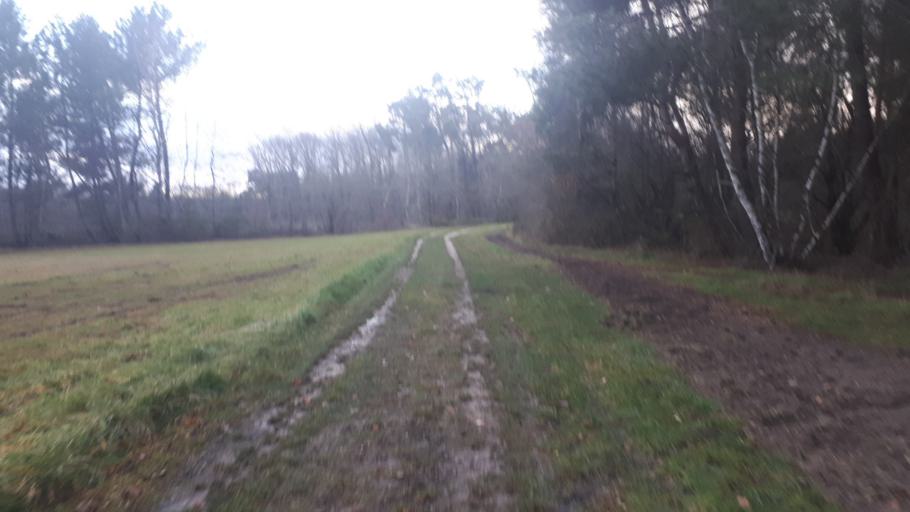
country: FR
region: Centre
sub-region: Departement du Loir-et-Cher
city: Saint-Romain-sur-Cher
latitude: 47.3457
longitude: 1.3951
